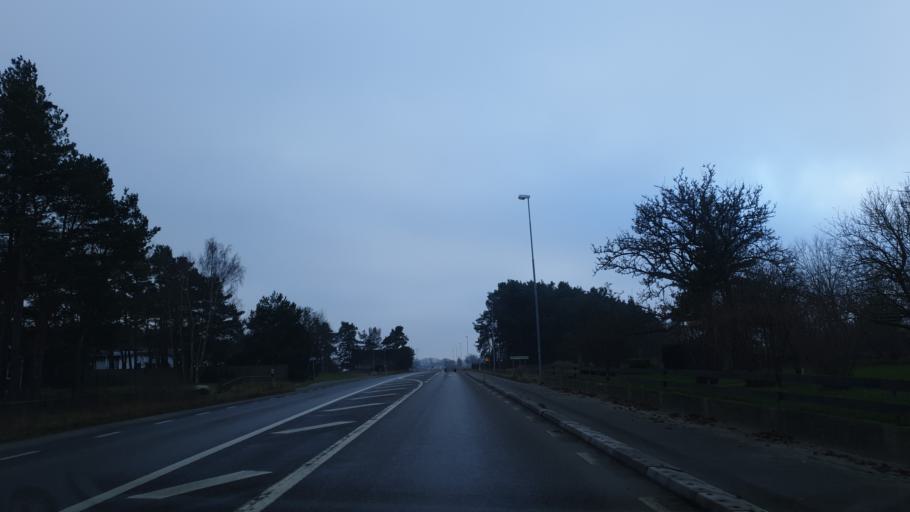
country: SE
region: Blekinge
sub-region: Solvesborgs Kommun
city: Soelvesborg
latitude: 56.0875
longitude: 14.6483
